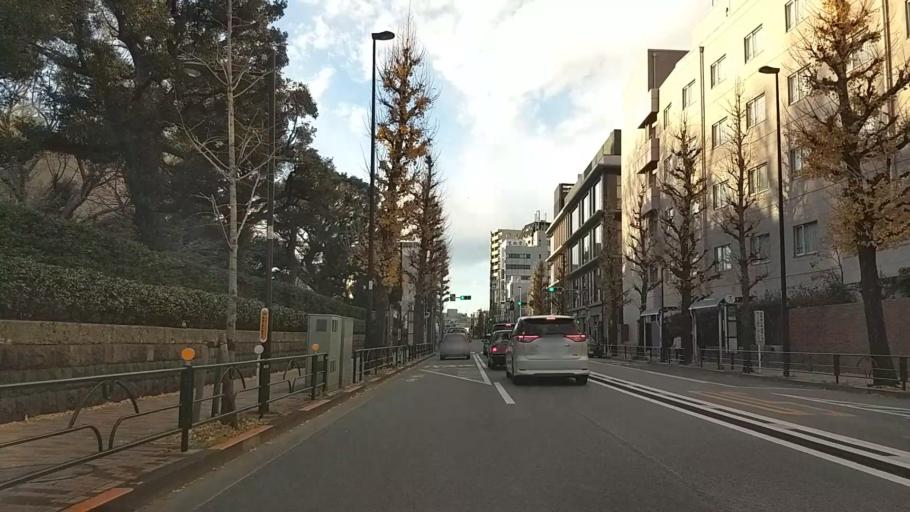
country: JP
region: Tokyo
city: Tokyo
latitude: 35.7208
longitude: 139.7084
